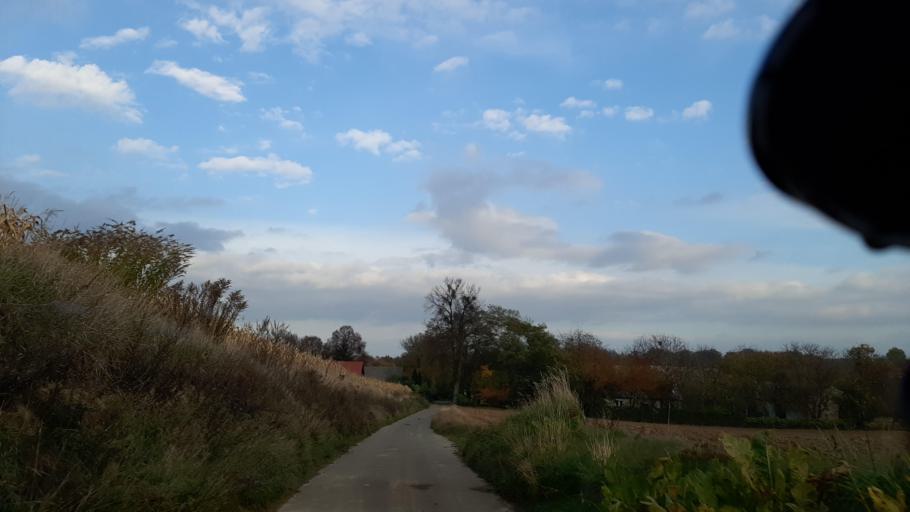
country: PL
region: Lublin Voivodeship
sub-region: Powiat pulawski
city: Markuszow
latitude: 51.3336
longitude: 22.2820
